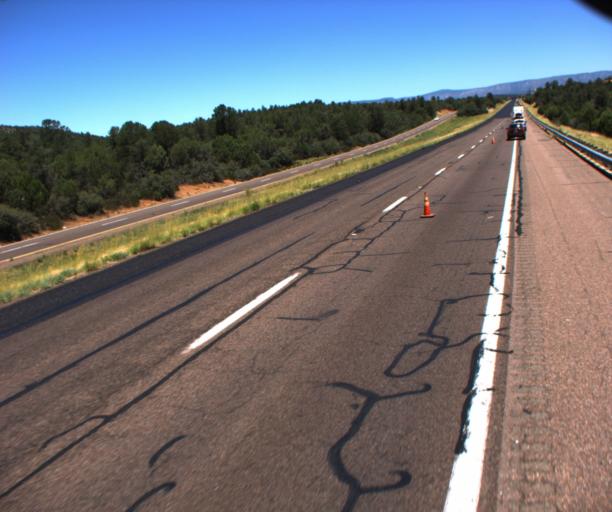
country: US
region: Arizona
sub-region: Gila County
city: Payson
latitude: 34.2076
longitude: -111.3313
